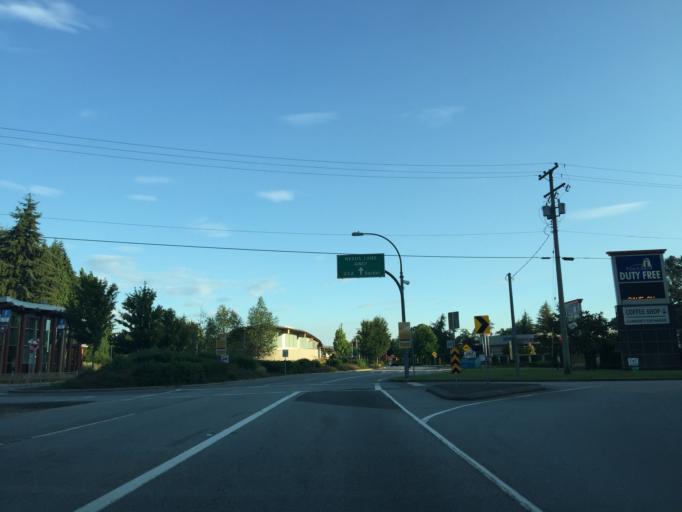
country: US
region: Washington
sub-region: Whatcom County
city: Blaine
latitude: 49.0077
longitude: -122.7577
